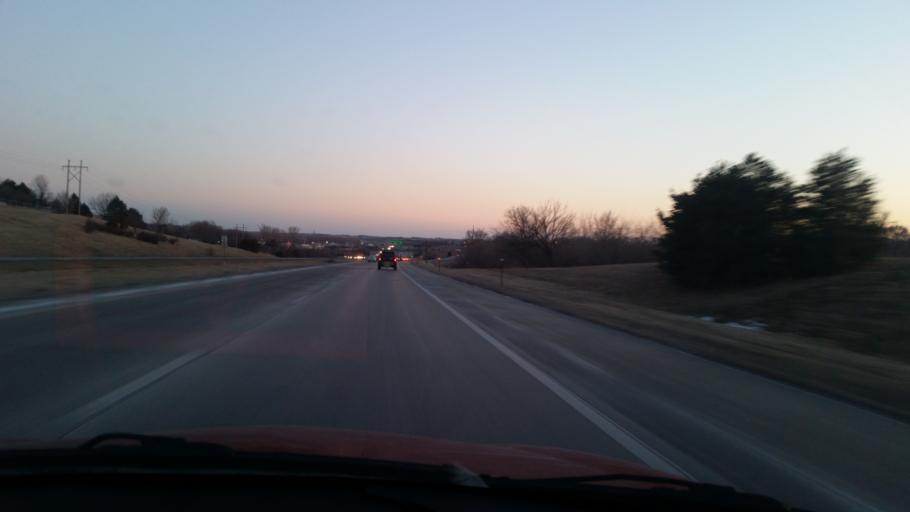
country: US
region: Nebraska
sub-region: Sarpy County
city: Offutt Air Force Base
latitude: 41.1667
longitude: -95.9392
